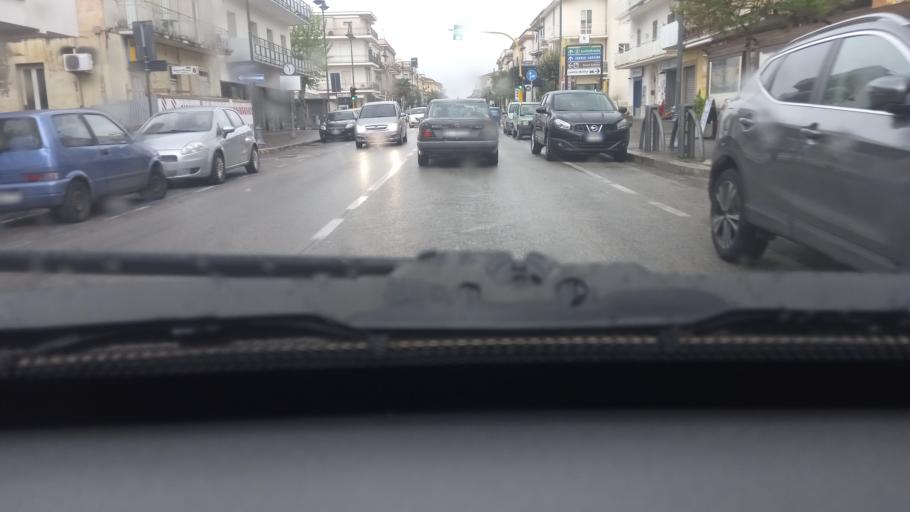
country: IT
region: Latium
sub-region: Provincia di Latina
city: Minturno
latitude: 41.2549
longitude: 13.7146
